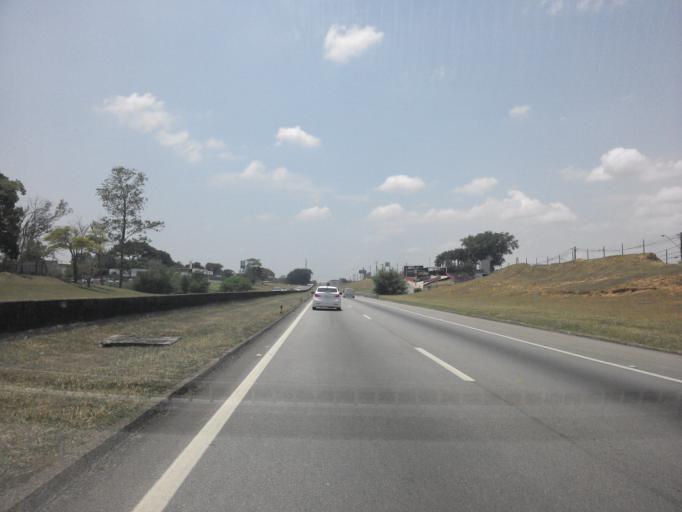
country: BR
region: Sao Paulo
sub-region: Cacapava
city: Cacapava
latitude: -23.1273
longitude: -45.7363
